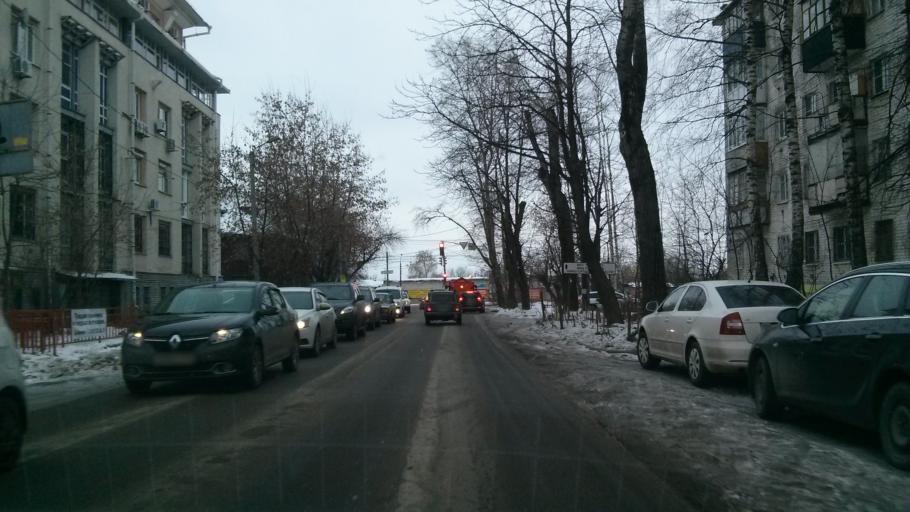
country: RU
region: Nizjnij Novgorod
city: Nizhniy Novgorod
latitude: 56.3104
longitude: 44.0052
